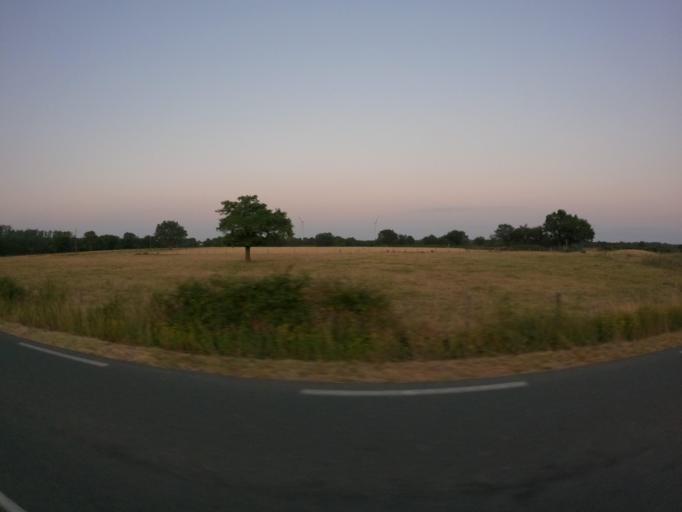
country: FR
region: Pays de la Loire
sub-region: Departement de Maine-et-Loire
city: Cande
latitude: 47.5958
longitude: -0.9993
